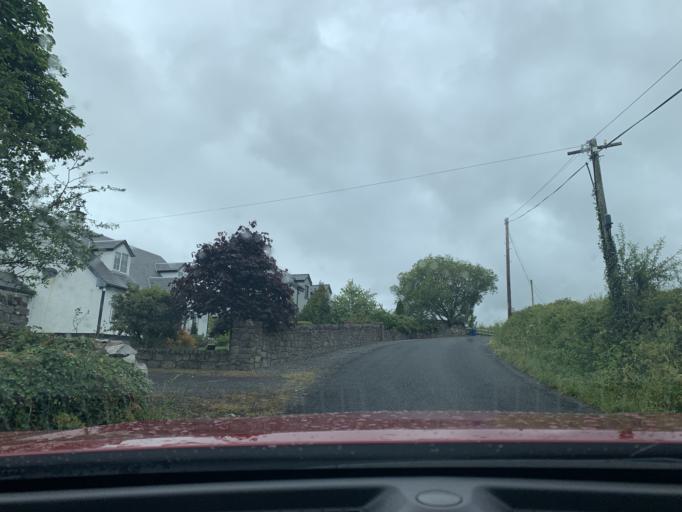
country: IE
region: Connaught
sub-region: Sligo
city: Sligo
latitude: 54.3050
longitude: -8.4563
